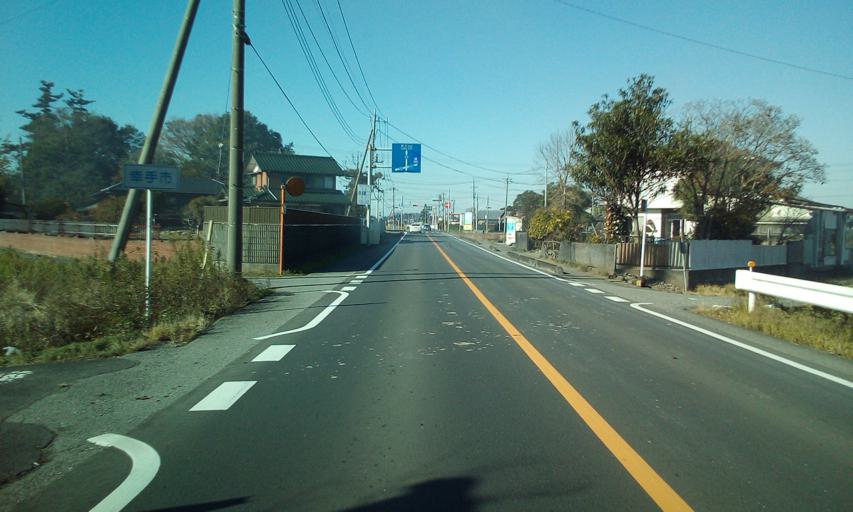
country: JP
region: Ibaraki
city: Sakai
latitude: 36.0496
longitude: 139.7796
